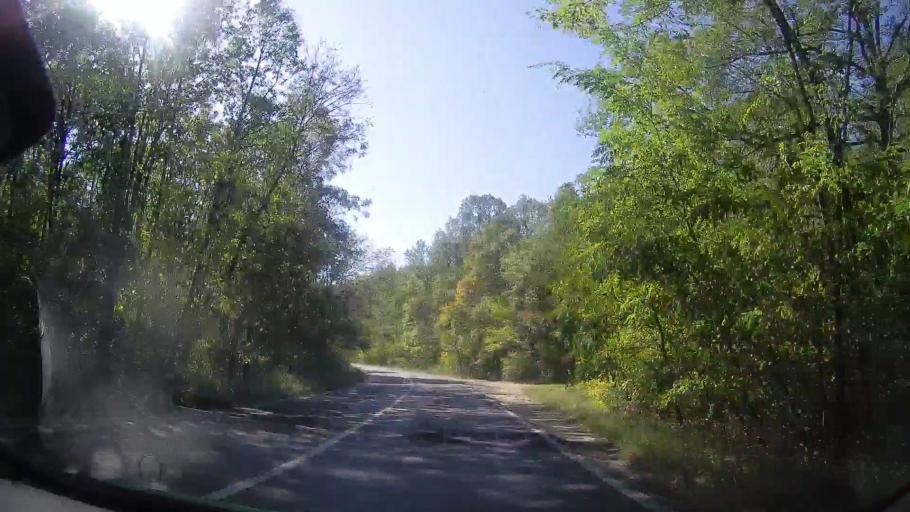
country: RO
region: Timis
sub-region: Comuna Barna
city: Barna
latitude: 45.7462
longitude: 21.9952
